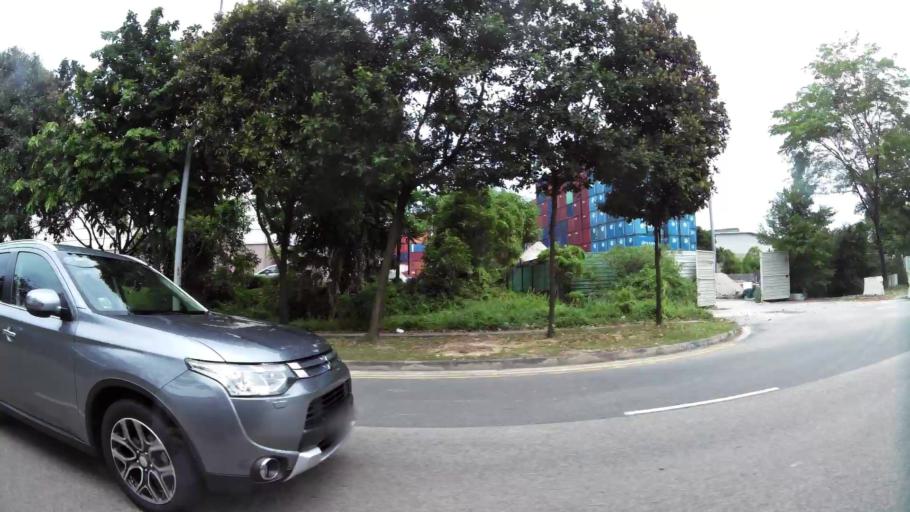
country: SG
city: Singapore
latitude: 1.3155
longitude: 103.6933
